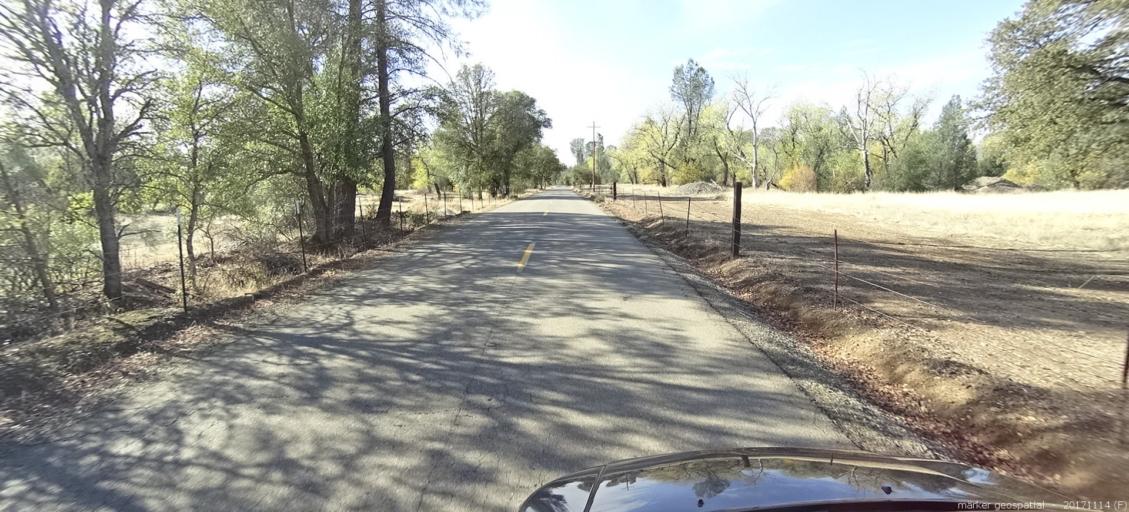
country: US
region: California
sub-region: Shasta County
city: Shasta
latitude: 40.3988
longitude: -122.5138
